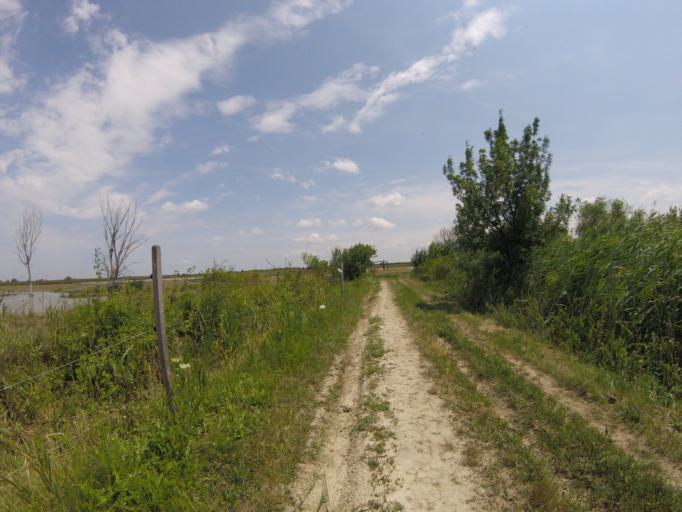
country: HU
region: Hajdu-Bihar
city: Hortobagy
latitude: 47.6090
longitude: 21.0719
